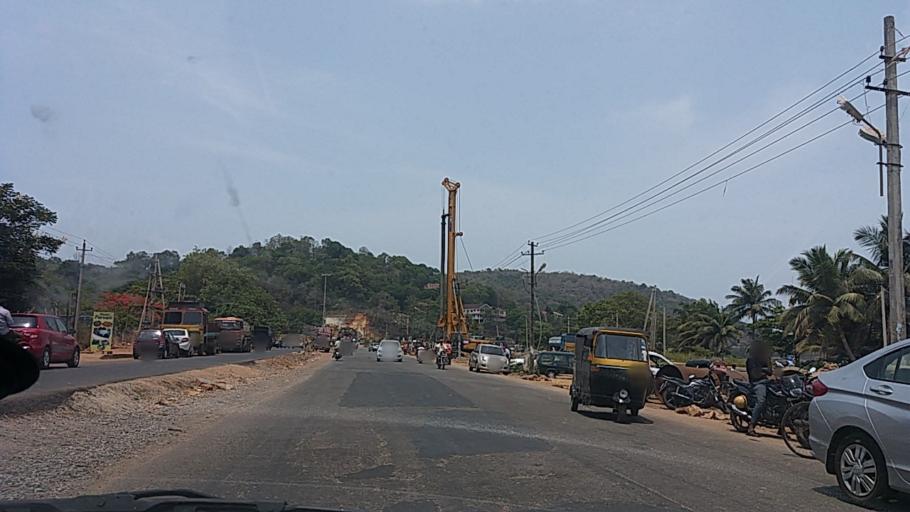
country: IN
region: Karnataka
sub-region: Uttar Kannada
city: Karwar
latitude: 14.8080
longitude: 74.1264
